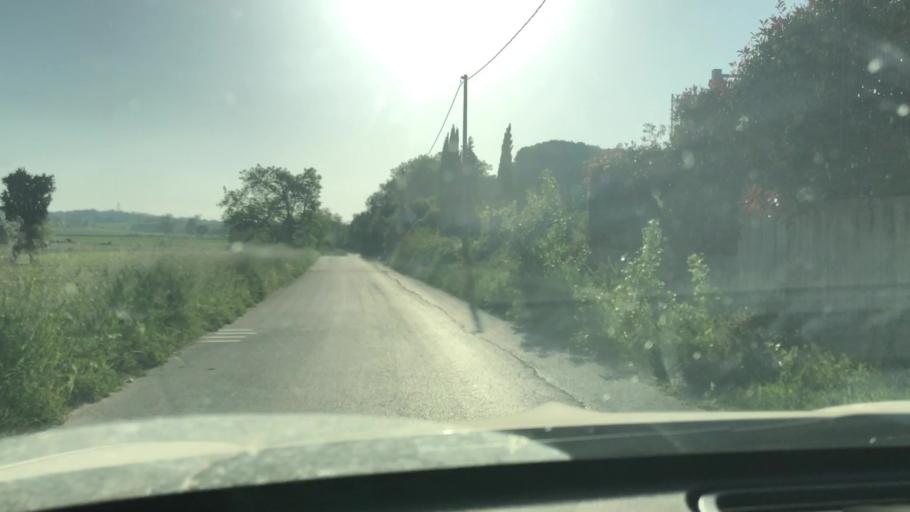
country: IT
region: Tuscany
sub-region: Province of Pisa
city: Cenaia
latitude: 43.5910
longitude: 10.5364
